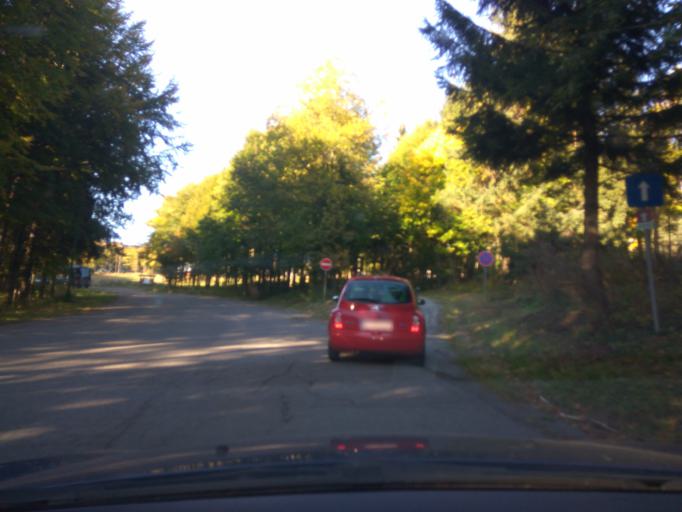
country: SK
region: Banskobystricky
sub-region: Okres Ziar nad Hronom
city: Kremnica
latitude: 48.7376
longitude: 18.9885
